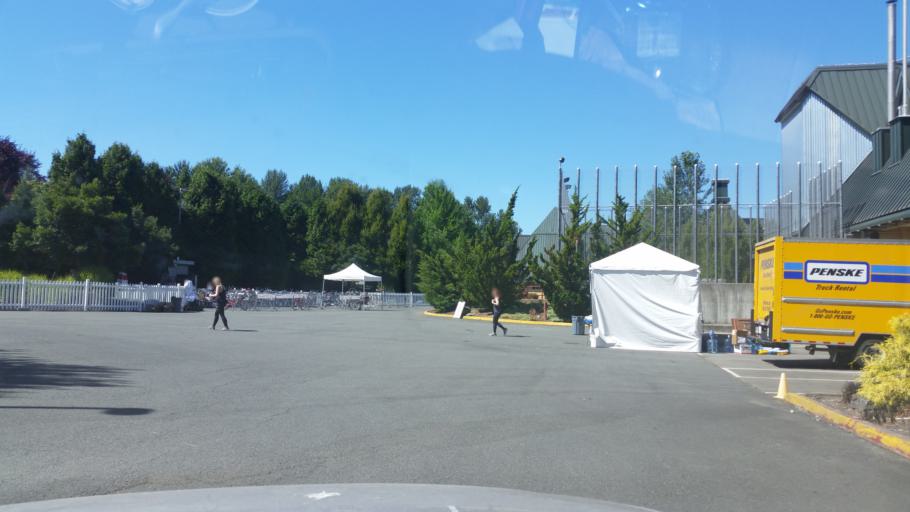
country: US
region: Washington
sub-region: King County
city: Woodinville
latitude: 47.7334
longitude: -122.1486
